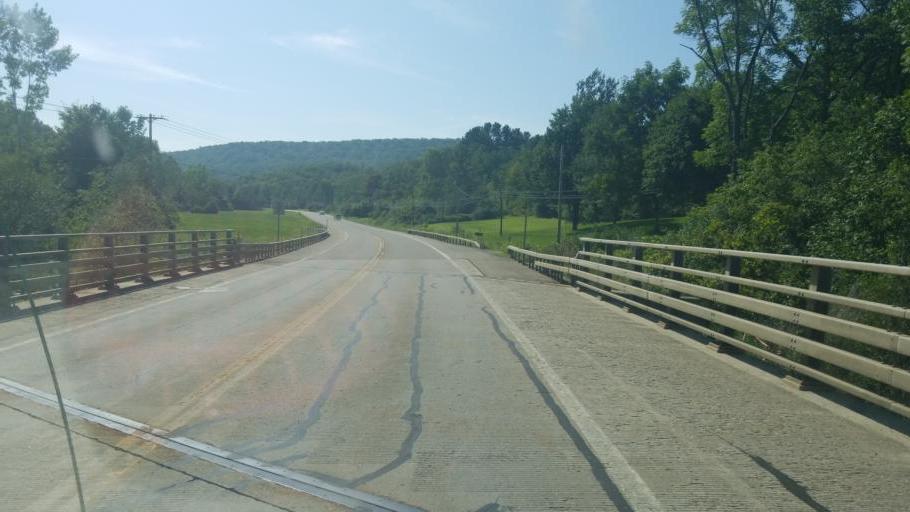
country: US
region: New York
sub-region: Allegany County
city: Wellsville
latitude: 42.1247
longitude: -77.9894
